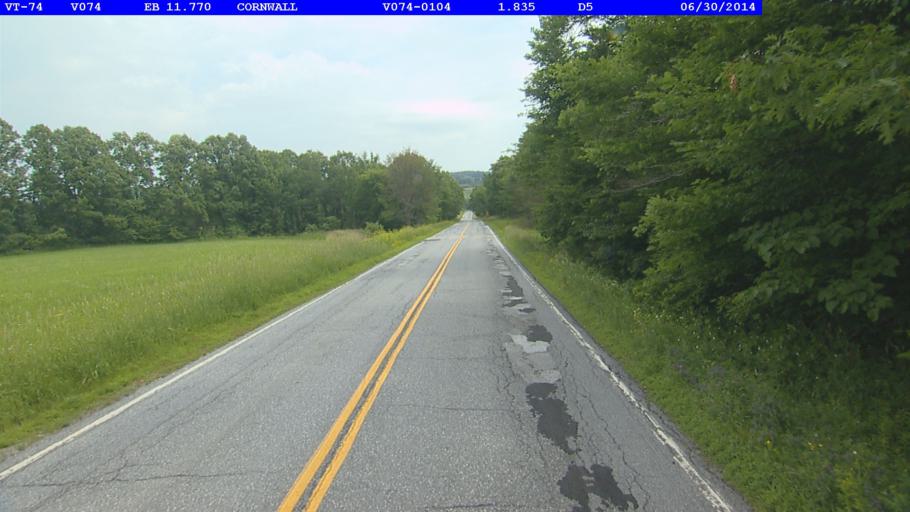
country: US
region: Vermont
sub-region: Addison County
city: Middlebury (village)
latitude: 43.9497
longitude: -73.2245
